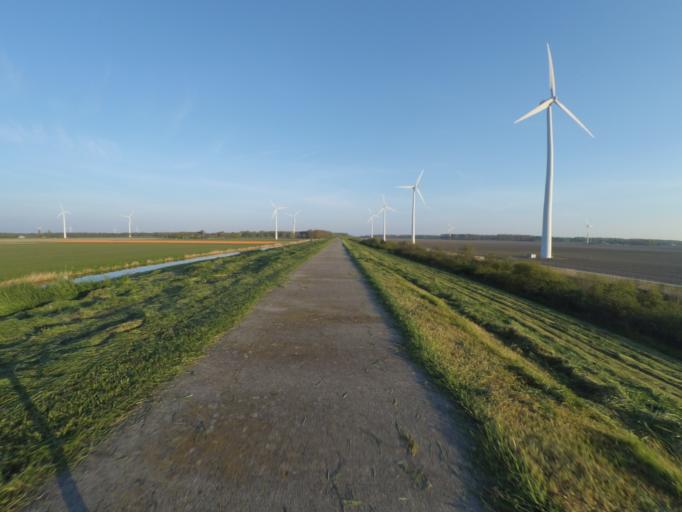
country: NL
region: Flevoland
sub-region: Gemeente Zeewolde
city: Zeewolde
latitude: 52.3944
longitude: 5.5162
